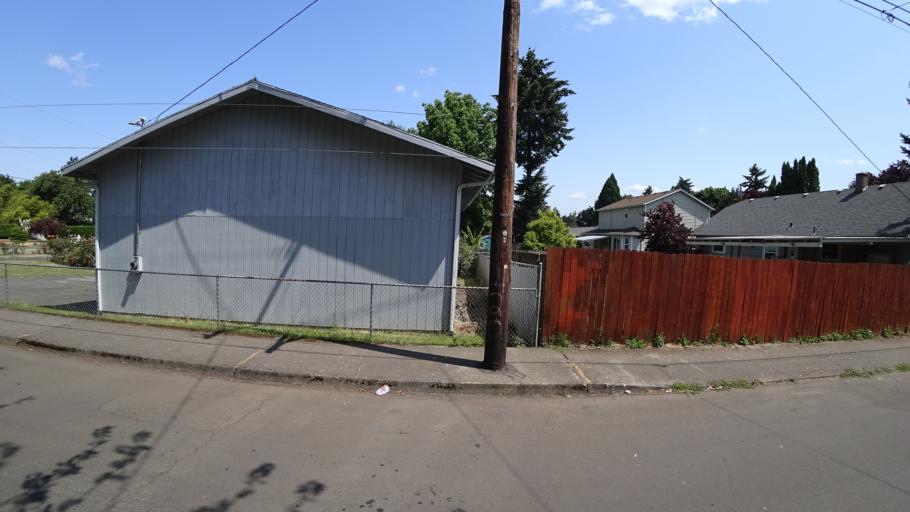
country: US
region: Oregon
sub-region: Washington County
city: West Haven
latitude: 45.5983
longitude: -122.7424
